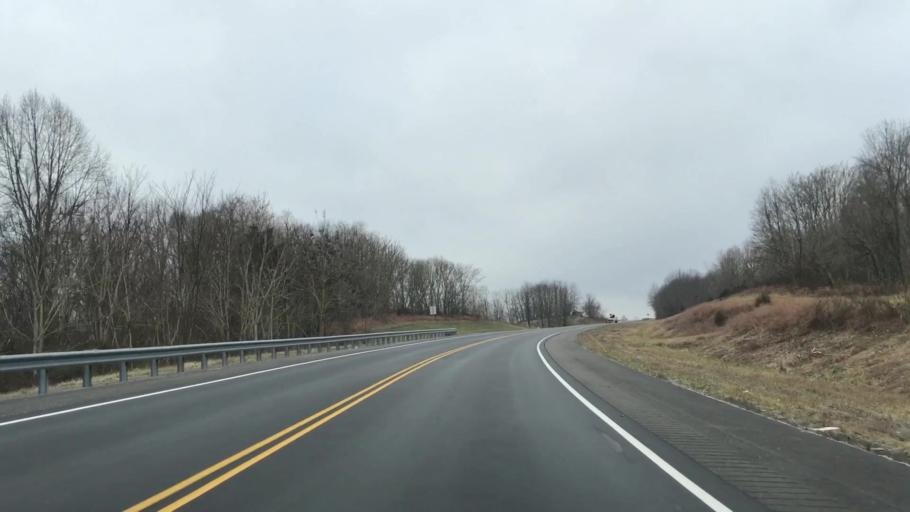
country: US
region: Kentucky
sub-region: Adair County
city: Columbia
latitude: 36.9724
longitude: -85.4228
